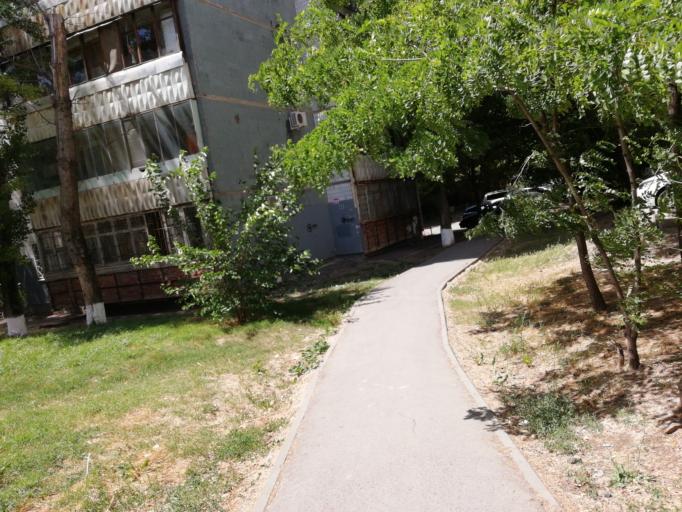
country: RU
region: Rostov
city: Severnyy
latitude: 47.2870
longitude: 39.7071
